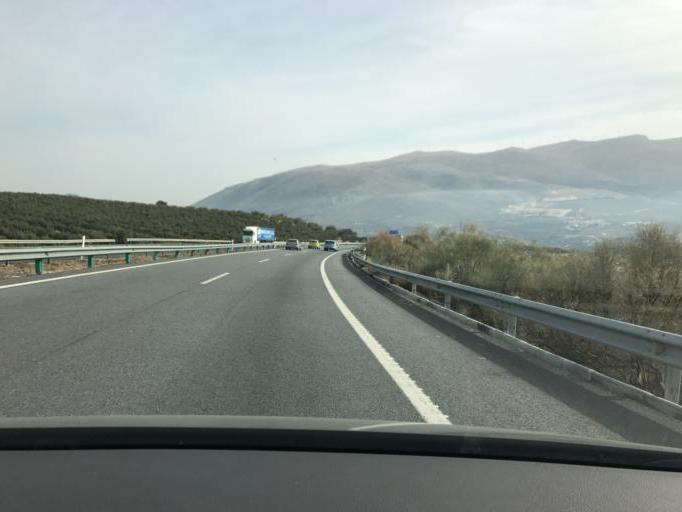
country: ES
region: Andalusia
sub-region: Provincia de Granada
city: Loja
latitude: 37.1457
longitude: -4.2418
